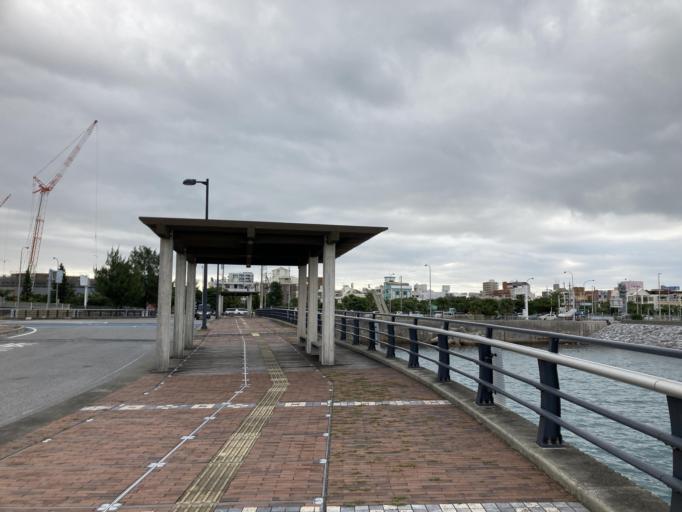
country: JP
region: Okinawa
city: Naha-shi
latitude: 26.2244
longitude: 127.6740
